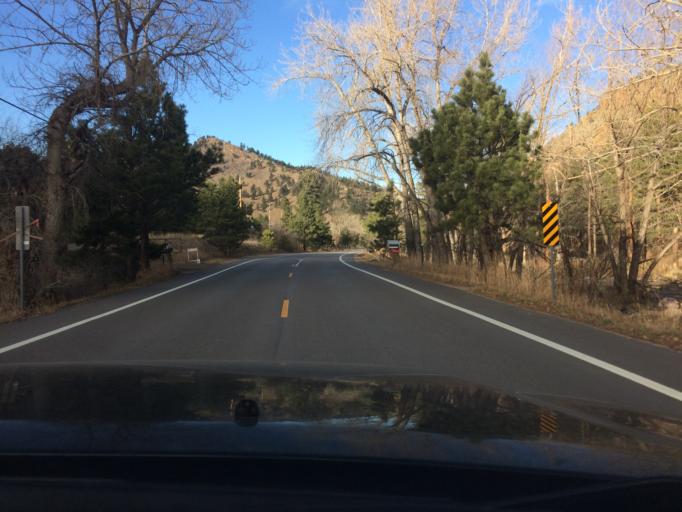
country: US
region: Colorado
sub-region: Boulder County
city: Boulder
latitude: 40.1196
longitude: -105.3070
